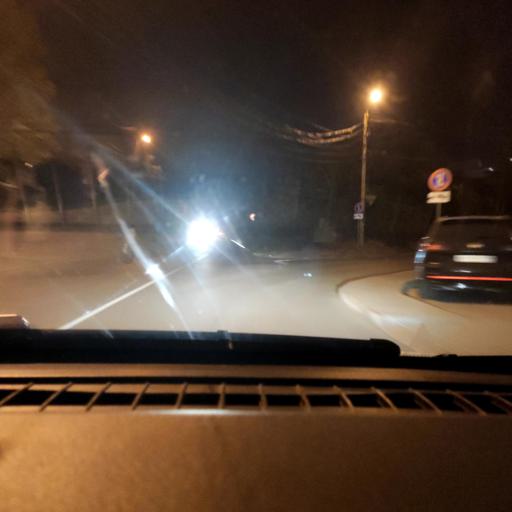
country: RU
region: Voronezj
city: Voronezh
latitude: 51.6691
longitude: 39.2135
